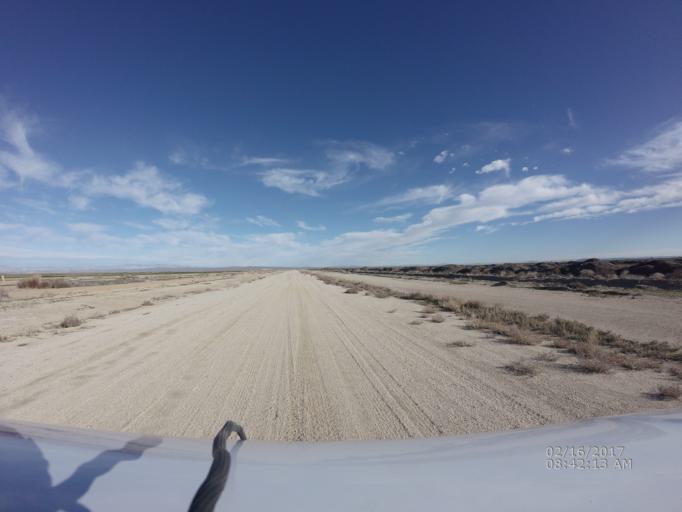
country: US
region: California
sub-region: Kern County
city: Edwards Air Force Base
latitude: 34.7656
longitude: -117.9875
